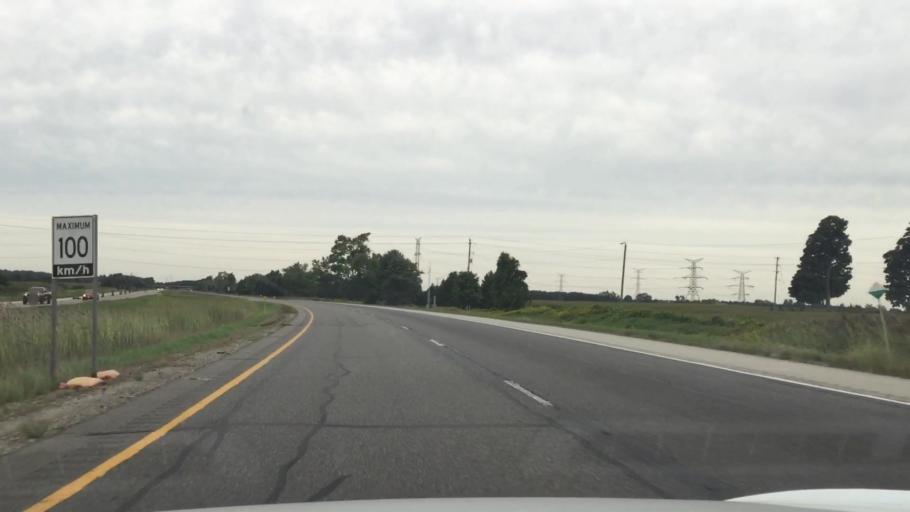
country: CA
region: Ontario
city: Delaware
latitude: 42.9535
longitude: -81.5279
